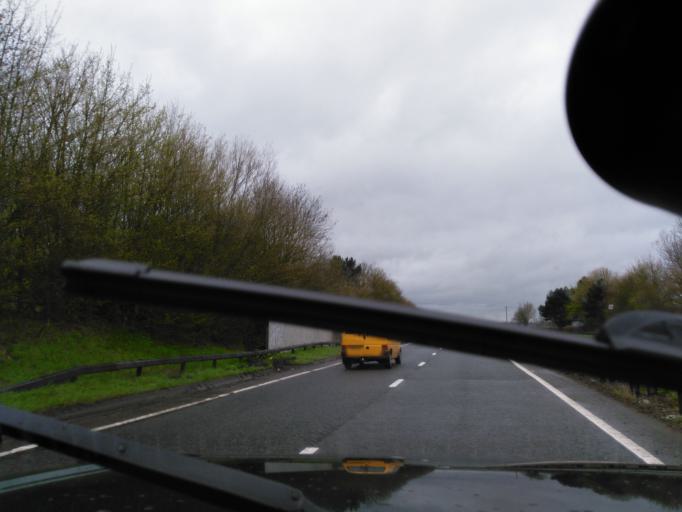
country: GB
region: England
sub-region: Wiltshire
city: Chapmanslade
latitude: 51.2673
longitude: -2.2801
